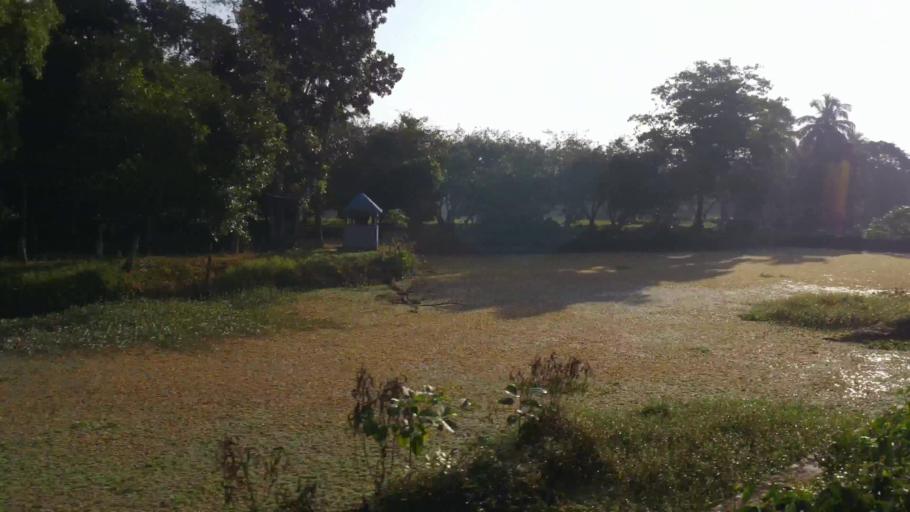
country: BD
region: Dhaka
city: Jamalpur
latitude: 24.9080
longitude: 89.9665
